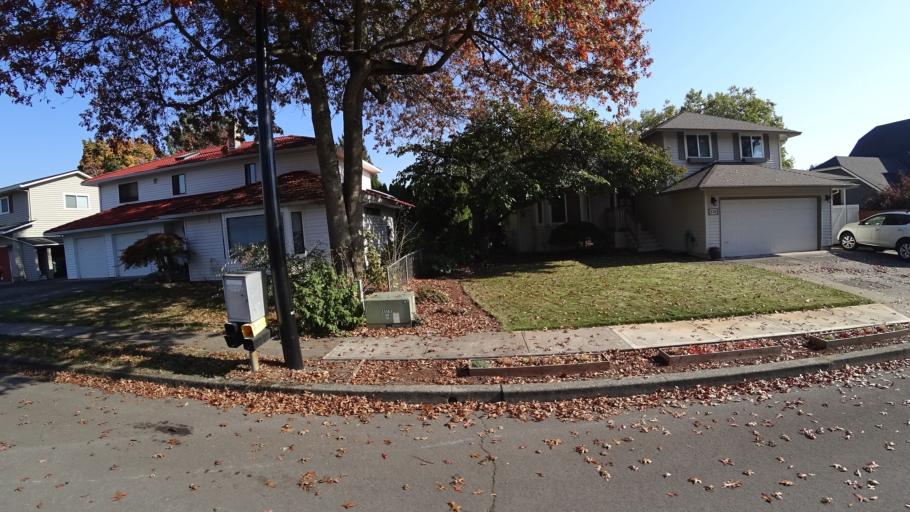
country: US
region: Oregon
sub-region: Multnomah County
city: Gresham
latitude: 45.4923
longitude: -122.4558
